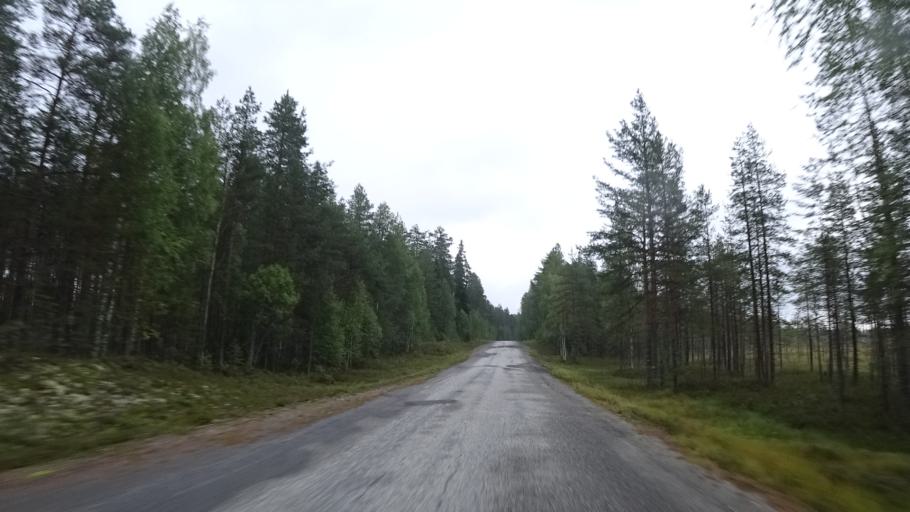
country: FI
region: North Karelia
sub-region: Joensuu
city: Ilomantsi
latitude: 63.2279
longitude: 30.8679
